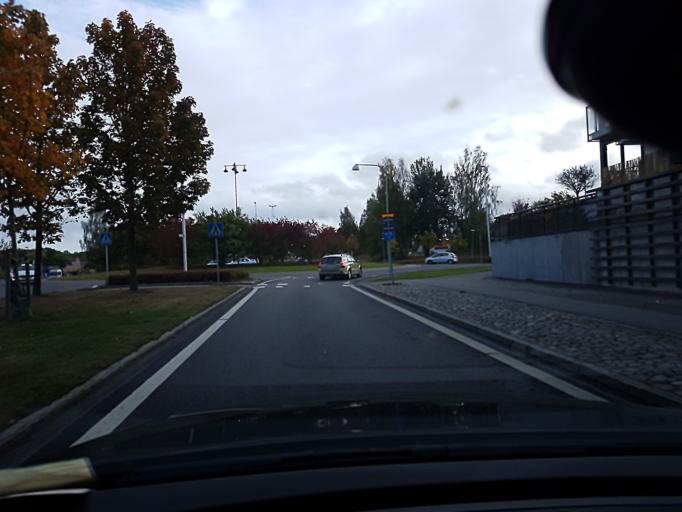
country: SE
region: Kronoberg
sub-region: Vaxjo Kommun
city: Vaexjoe
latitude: 56.8586
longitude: 14.8211
